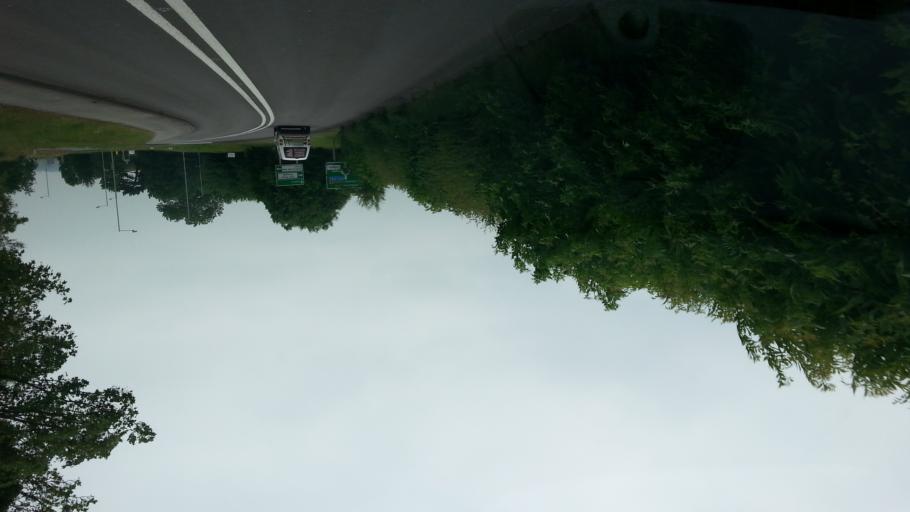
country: GB
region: England
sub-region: Staffordshire
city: Uttoxeter
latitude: 52.8614
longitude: -1.7673
